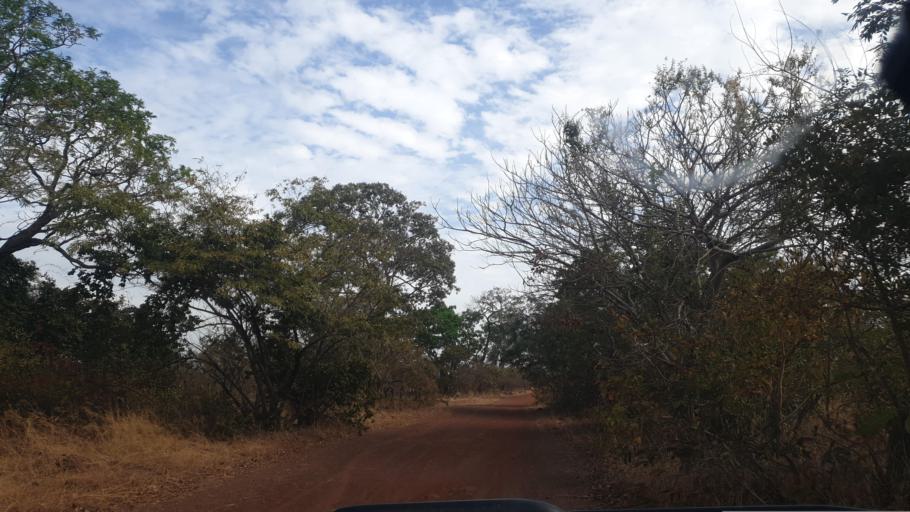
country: ML
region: Sikasso
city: Yanfolila
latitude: 11.3948
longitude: -8.0201
